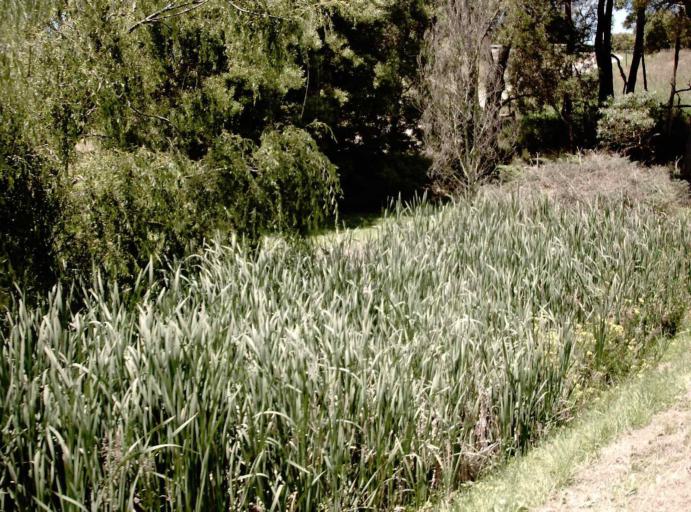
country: AU
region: Victoria
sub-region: Bass Coast
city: North Wonthaggi
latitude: -38.7207
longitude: 146.1205
